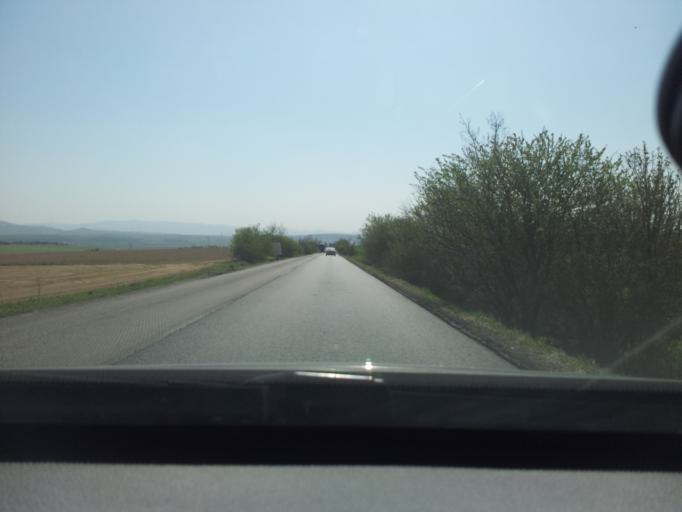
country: SK
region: Nitriansky
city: Banovce nad Bebravou
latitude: 48.7625
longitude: 18.1934
